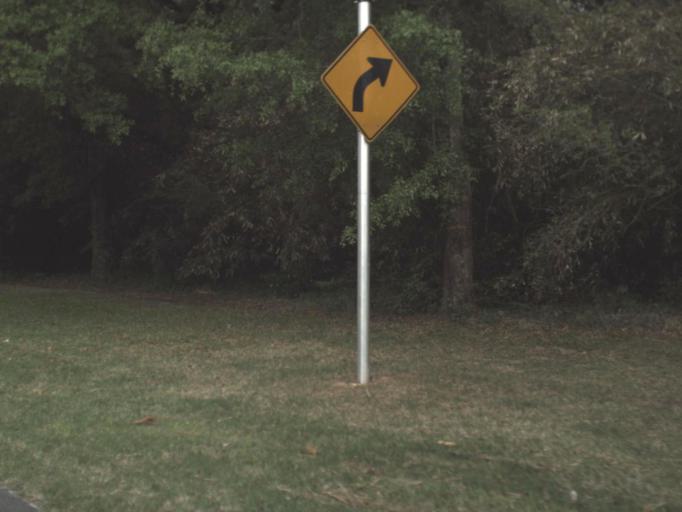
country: US
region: Florida
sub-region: Escambia County
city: East Pensacola Heights
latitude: 30.4456
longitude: -87.1829
